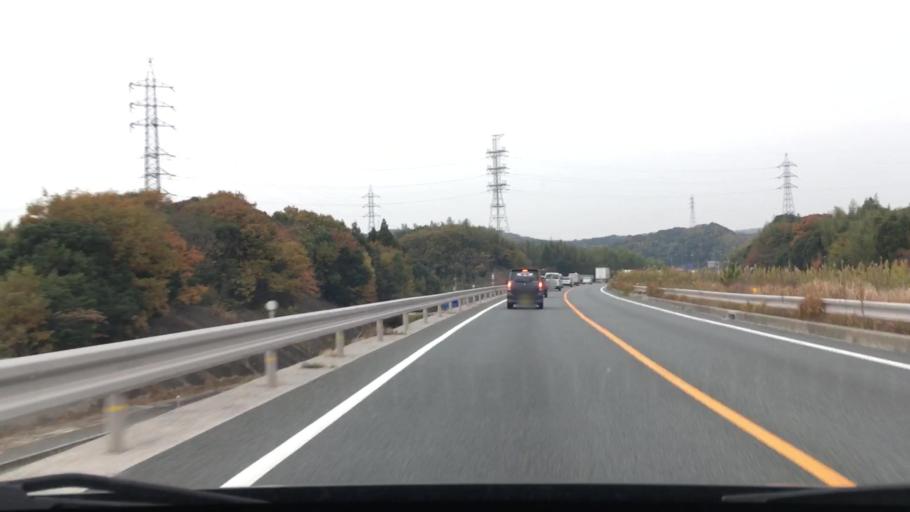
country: JP
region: Yamaguchi
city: Onoda
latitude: 34.0443
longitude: 131.1747
